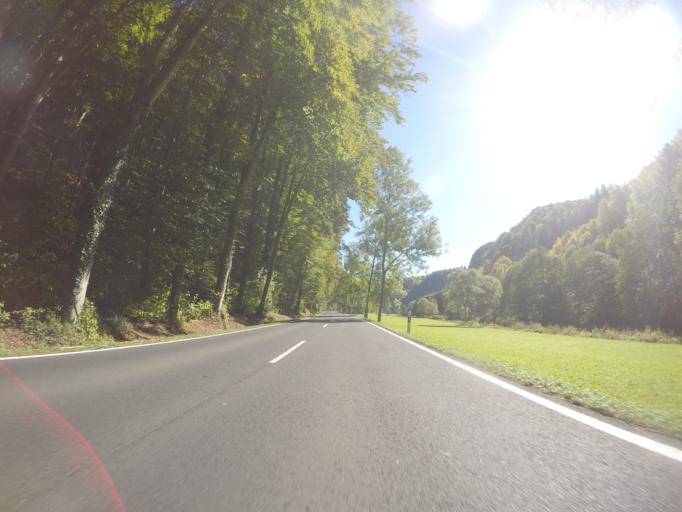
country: DE
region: Bavaria
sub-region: Upper Franconia
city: Gossweinstein
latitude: 49.7799
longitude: 11.2924
